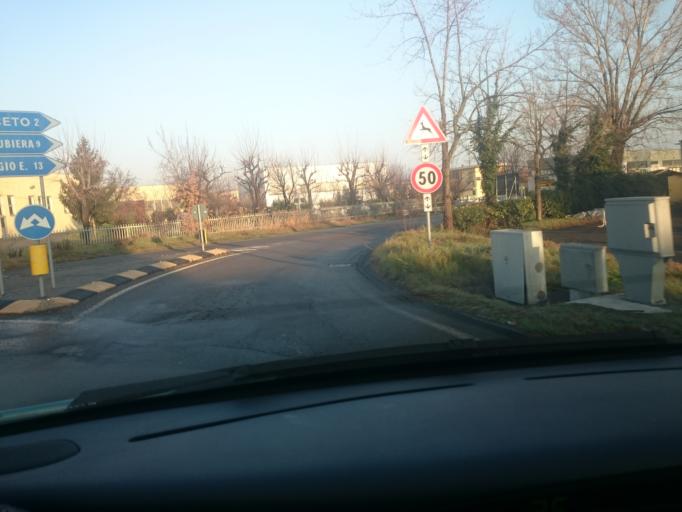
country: IT
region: Emilia-Romagna
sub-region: Provincia di Reggio Emilia
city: Scandiano
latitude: 44.6007
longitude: 10.7042
